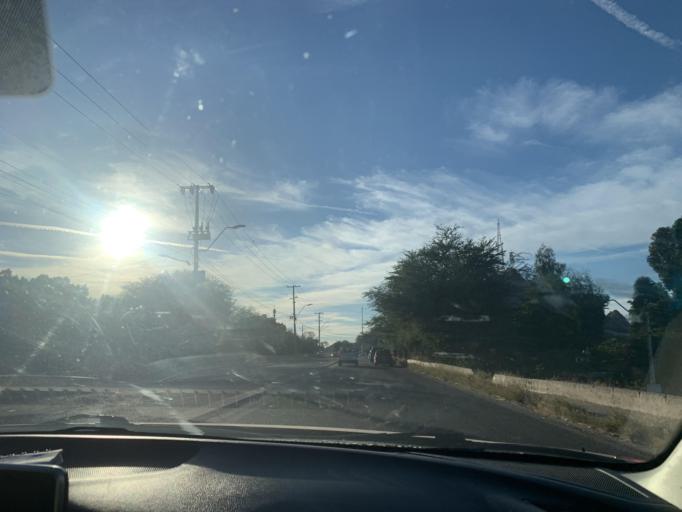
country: MX
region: Sonora
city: Hermosillo
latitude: 29.0722
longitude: -110.9401
